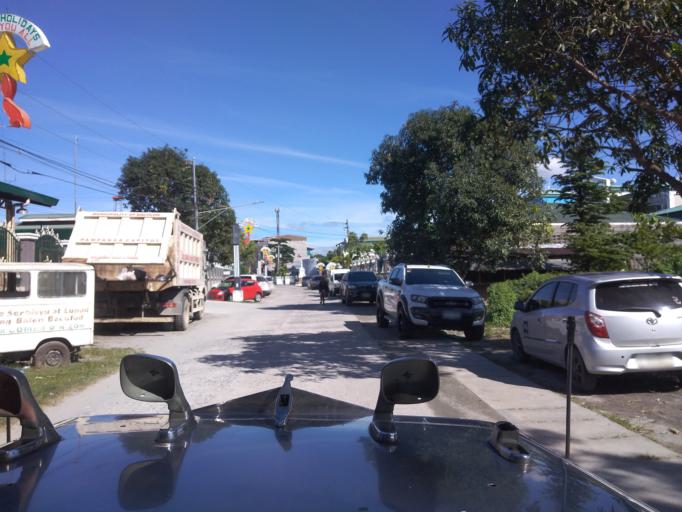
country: PH
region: Central Luzon
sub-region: Province of Pampanga
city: Bacolor
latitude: 14.9970
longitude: 120.6512
